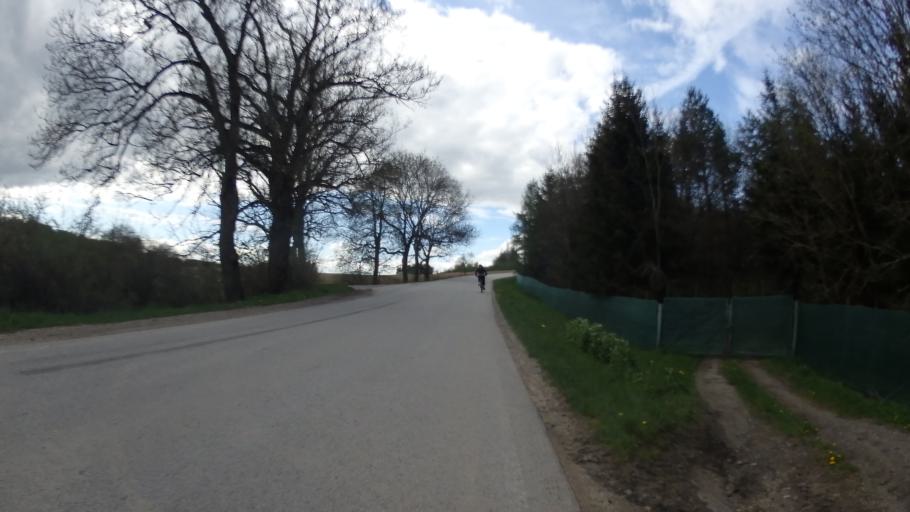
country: CZ
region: Vysocina
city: Merin
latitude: 49.3642
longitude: 15.9021
